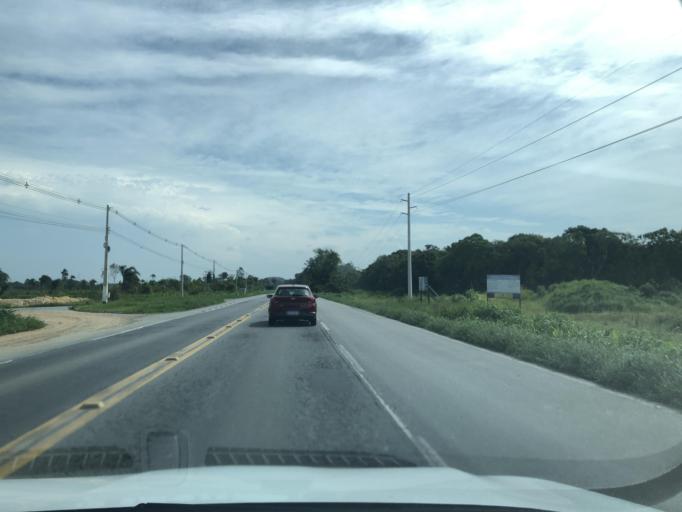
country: BR
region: Santa Catarina
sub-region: Sao Francisco Do Sul
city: Sao Francisco do Sul
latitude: -26.3405
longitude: -48.6555
